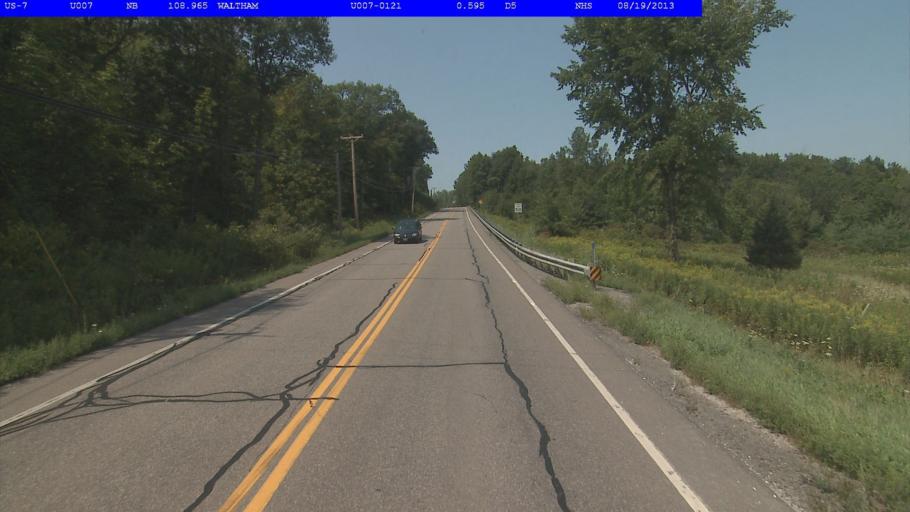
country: US
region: Vermont
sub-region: Addison County
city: Vergennes
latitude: 44.1540
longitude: -73.2182
